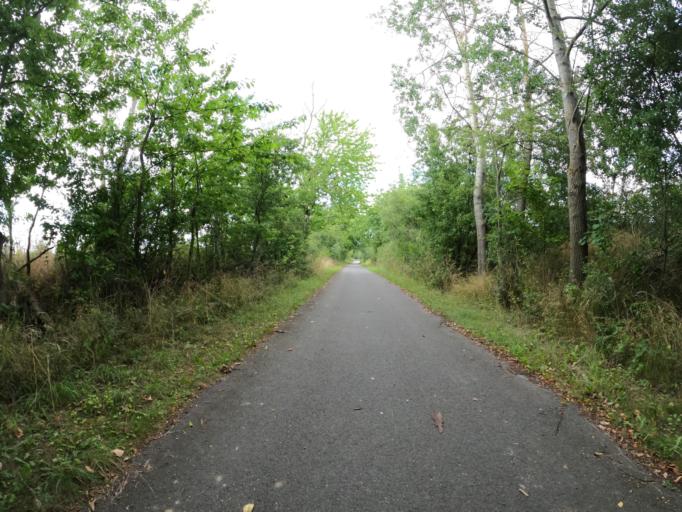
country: DE
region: Mecklenburg-Vorpommern
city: Woldegk
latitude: 53.3704
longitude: 13.5890
